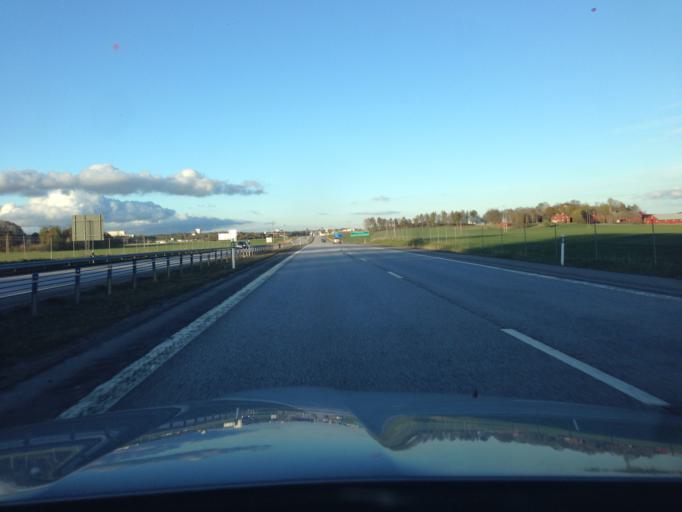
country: SE
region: Soedermanland
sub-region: Nykopings Kommun
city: Nykoping
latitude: 58.7464
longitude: 16.9527
